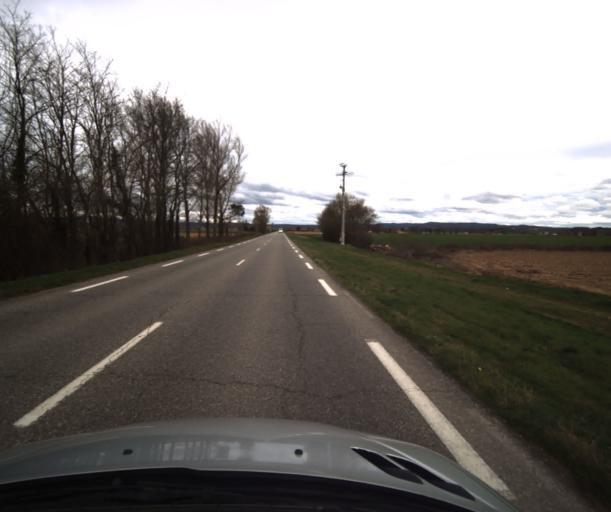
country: FR
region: Midi-Pyrenees
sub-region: Departement du Tarn-et-Garonne
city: Negrepelisse
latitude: 44.0732
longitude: 1.5656
